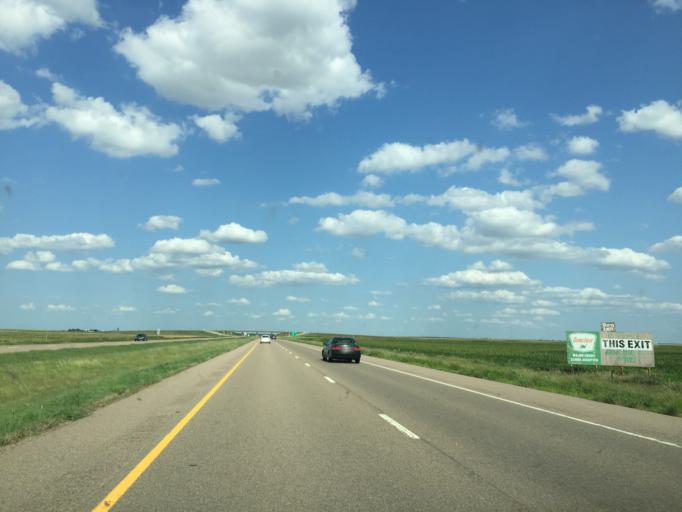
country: US
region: Kansas
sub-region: Gove County
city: Gove
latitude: 39.0971
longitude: -100.3801
